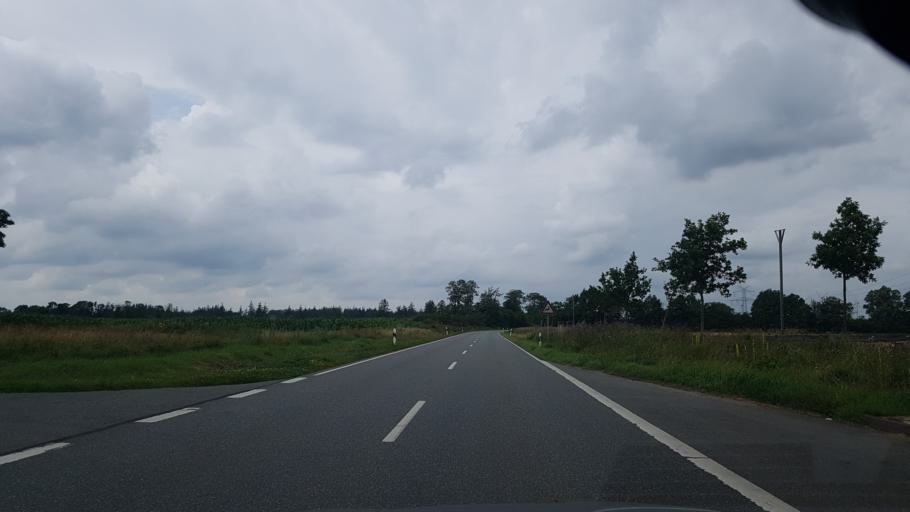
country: DE
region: Schleswig-Holstein
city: Osterby
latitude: 54.8184
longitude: 9.2248
